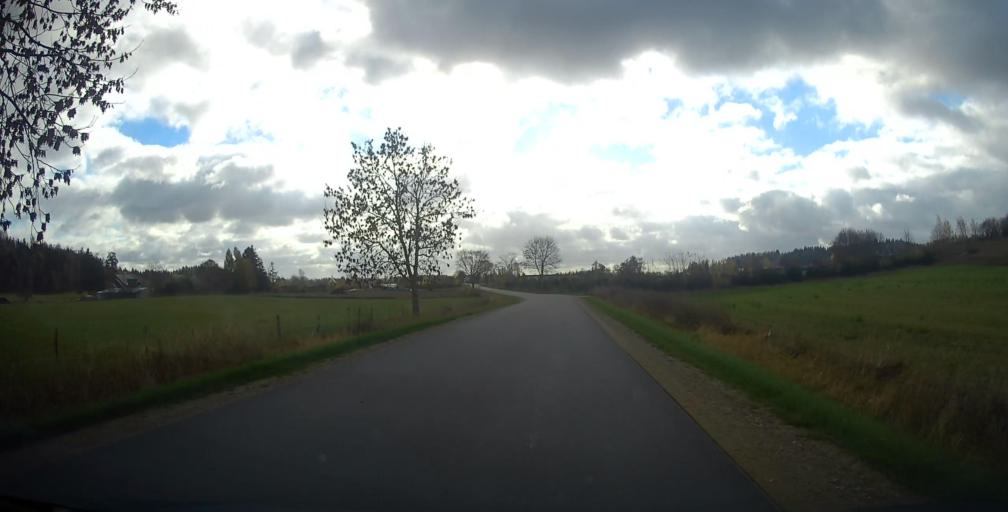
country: PL
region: Podlasie
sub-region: Suwalki
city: Suwalki
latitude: 54.2986
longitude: 22.8784
